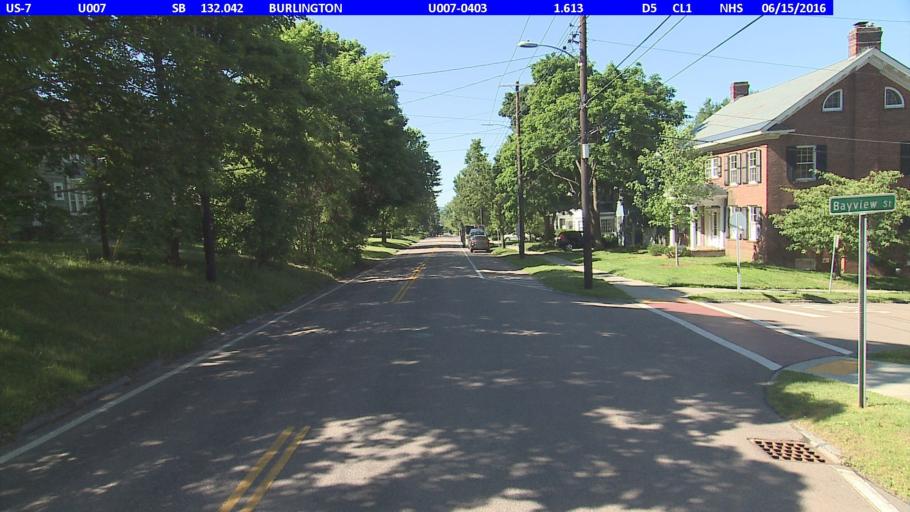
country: US
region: Vermont
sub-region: Chittenden County
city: Burlington
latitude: 44.4689
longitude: -73.2053
